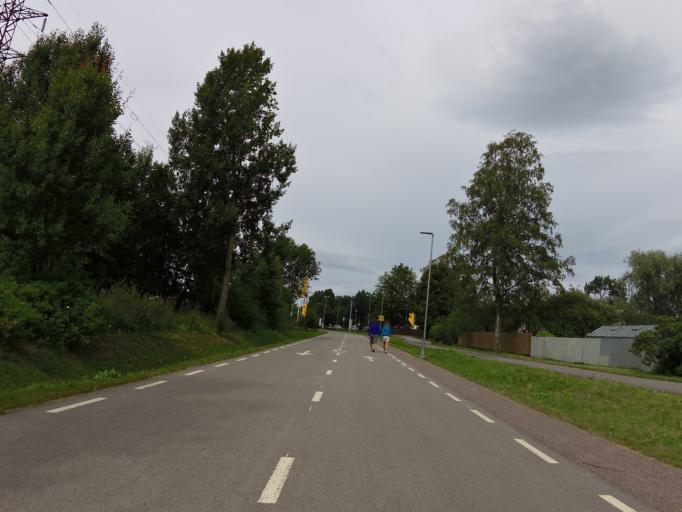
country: EE
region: Harju
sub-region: Tallinna linn
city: Tallinn
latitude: 59.4279
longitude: 24.6838
